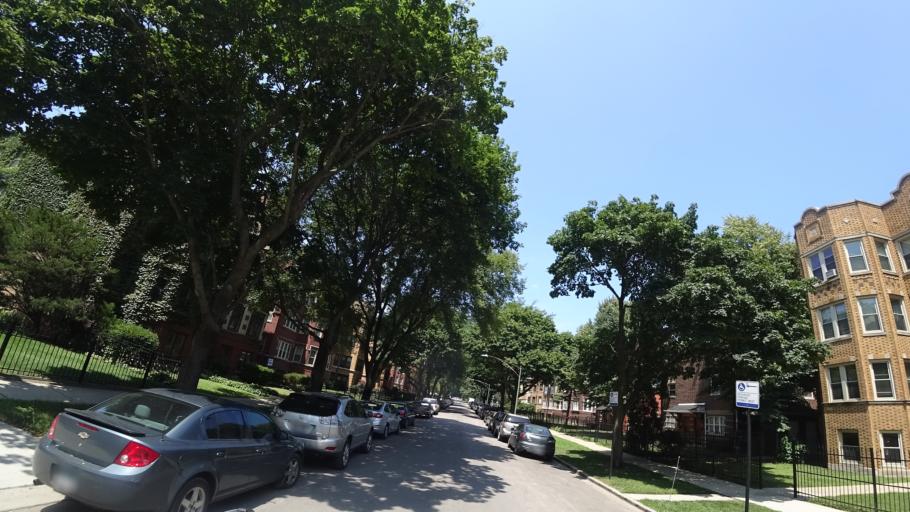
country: US
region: Illinois
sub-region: Cook County
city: Chicago
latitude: 41.7720
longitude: -87.5752
